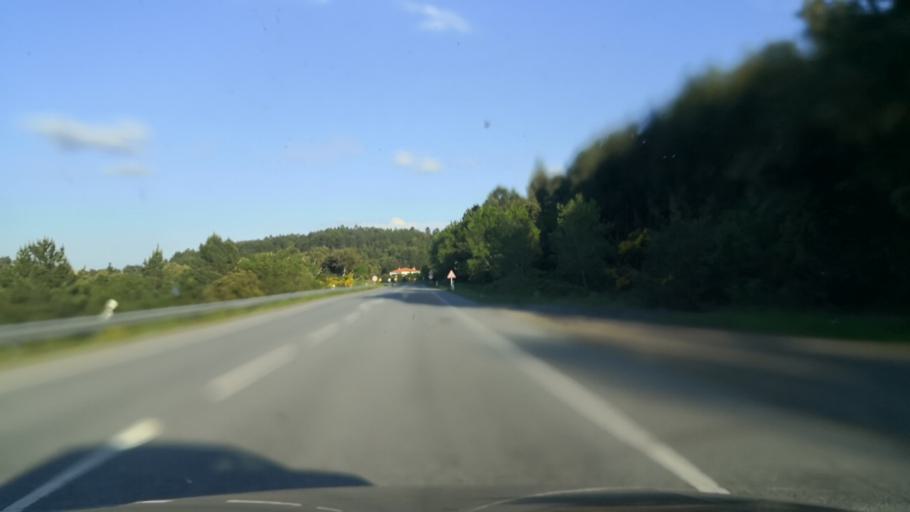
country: PT
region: Portalegre
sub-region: Marvao
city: Marvao
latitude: 39.3702
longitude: -7.3467
